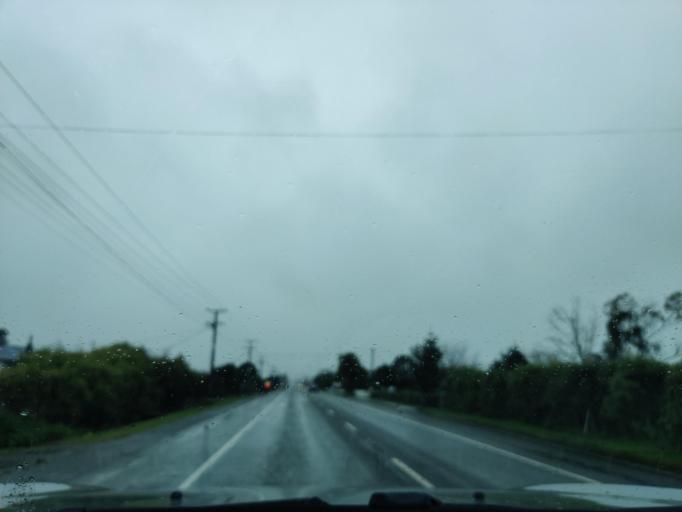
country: NZ
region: Hawke's Bay
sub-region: Hastings District
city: Hastings
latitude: -39.9913
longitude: 176.5336
